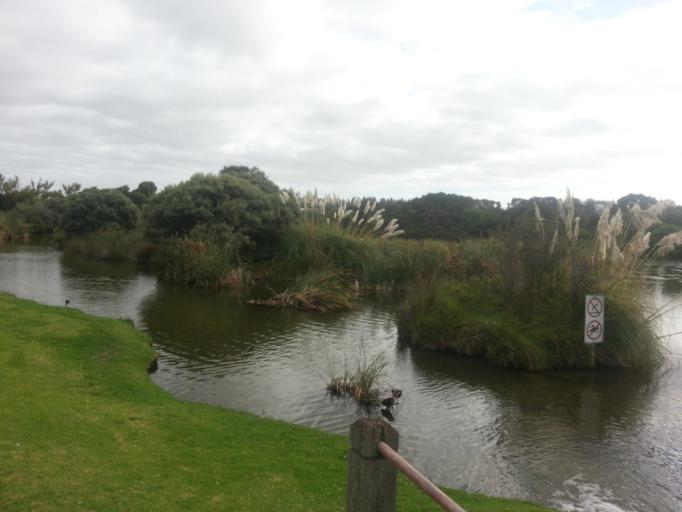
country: AU
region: Victoria
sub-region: Warrnambool
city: Warrnambool
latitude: -38.3929
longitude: 142.4779
